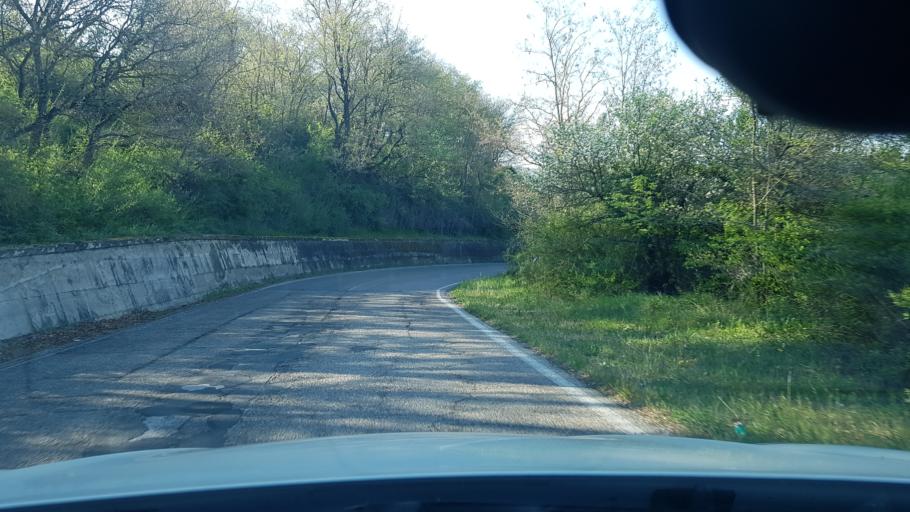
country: IT
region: Umbria
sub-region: Provincia di Perugia
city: Magione
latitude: 43.1643
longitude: 12.1896
